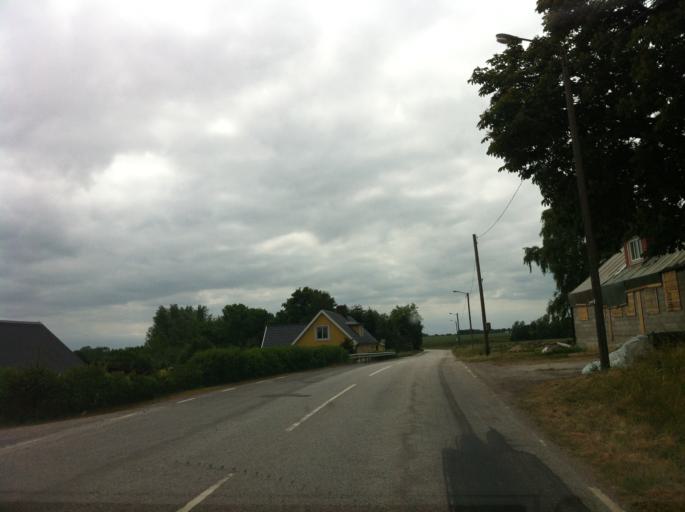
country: SE
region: Skane
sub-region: Eslovs Kommun
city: Eslov
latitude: 55.8378
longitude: 13.3298
